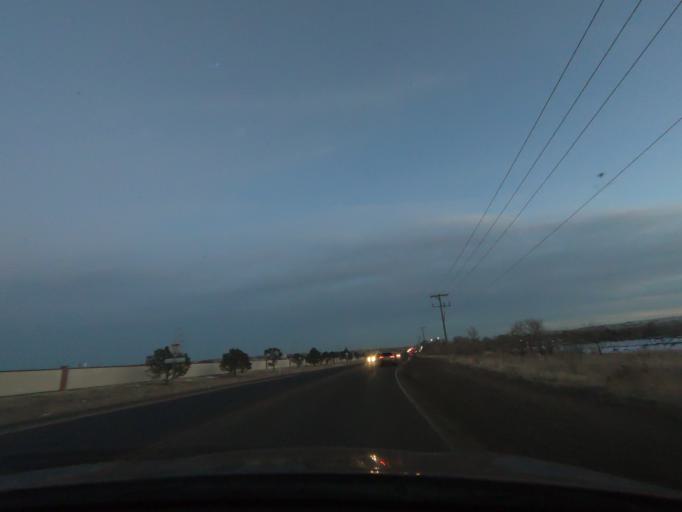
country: US
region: Colorado
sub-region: El Paso County
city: Stratmoor
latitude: 38.7767
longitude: -104.7703
